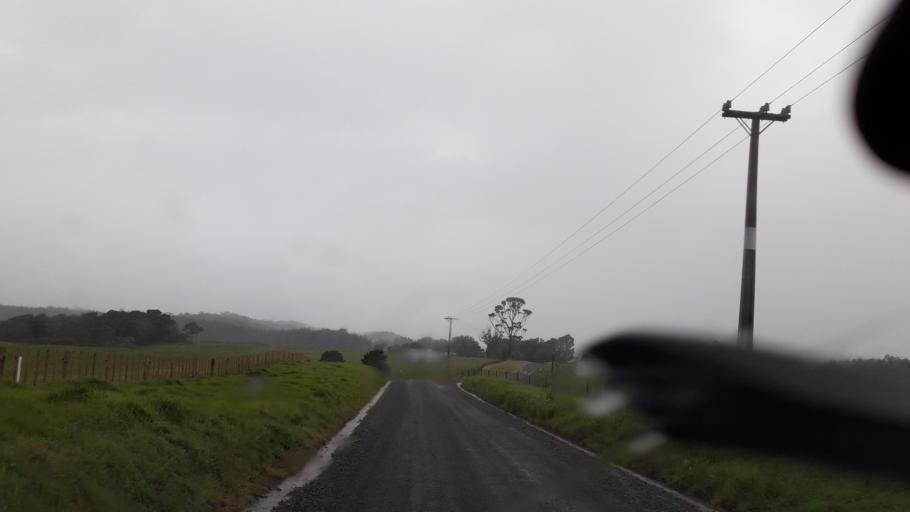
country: NZ
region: Northland
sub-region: Far North District
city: Kerikeri
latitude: -35.1487
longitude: 174.0388
